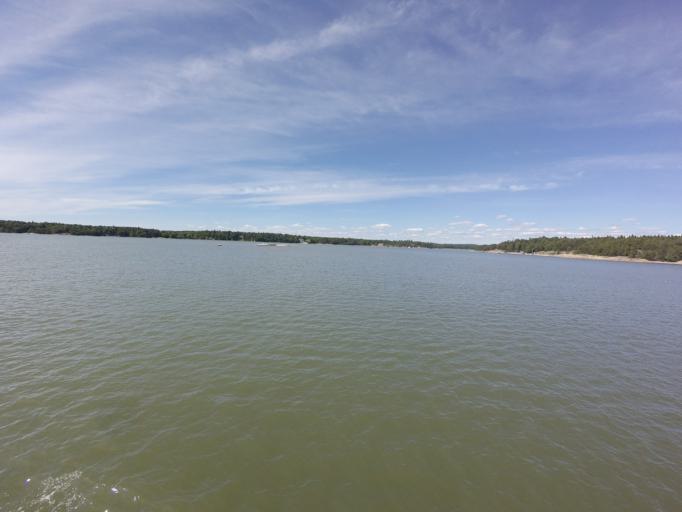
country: FI
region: Varsinais-Suomi
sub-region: Turku
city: Raisio
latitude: 60.4085
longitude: 22.1377
